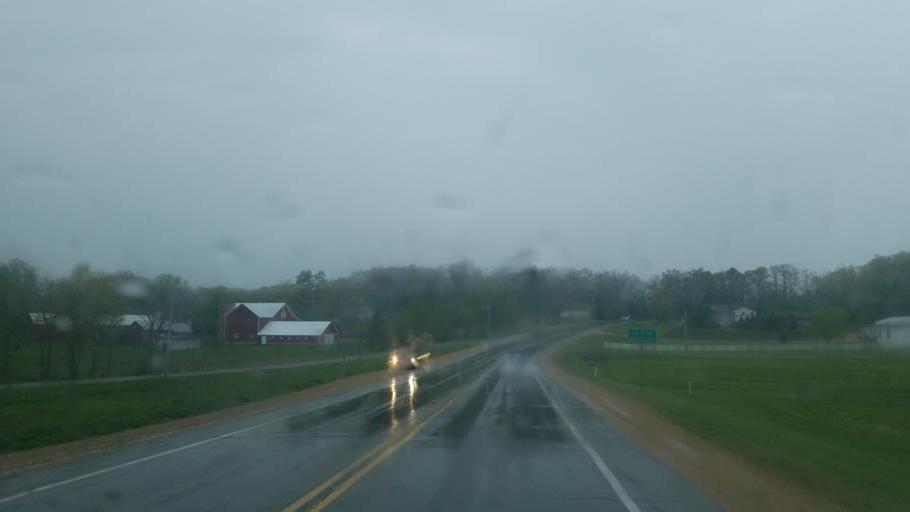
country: US
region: Wisconsin
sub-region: Sauk County
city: Reedsburg
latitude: 43.5818
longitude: -90.1216
